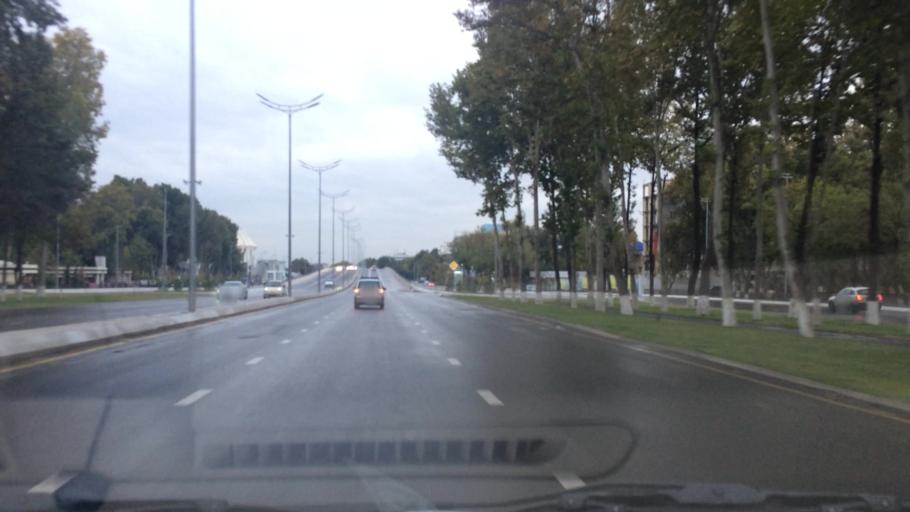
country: UZ
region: Toshkent Shahri
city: Tashkent
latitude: 41.2857
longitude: 69.2159
